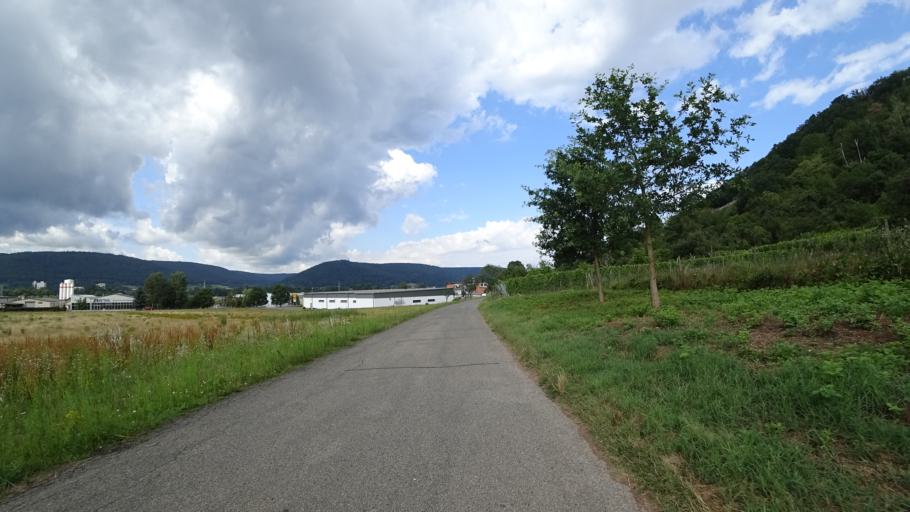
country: DE
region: Bavaria
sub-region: Regierungsbezirk Unterfranken
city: Grossheubach
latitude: 49.7207
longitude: 9.2344
